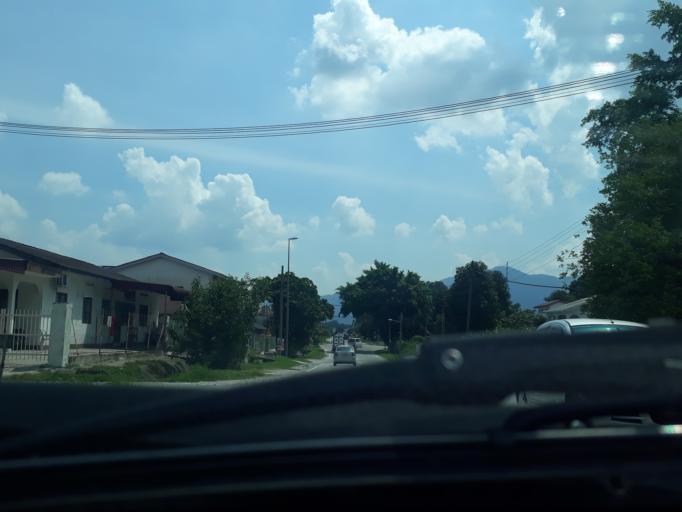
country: MY
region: Perak
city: Ipoh
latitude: 4.5774
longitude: 101.0866
